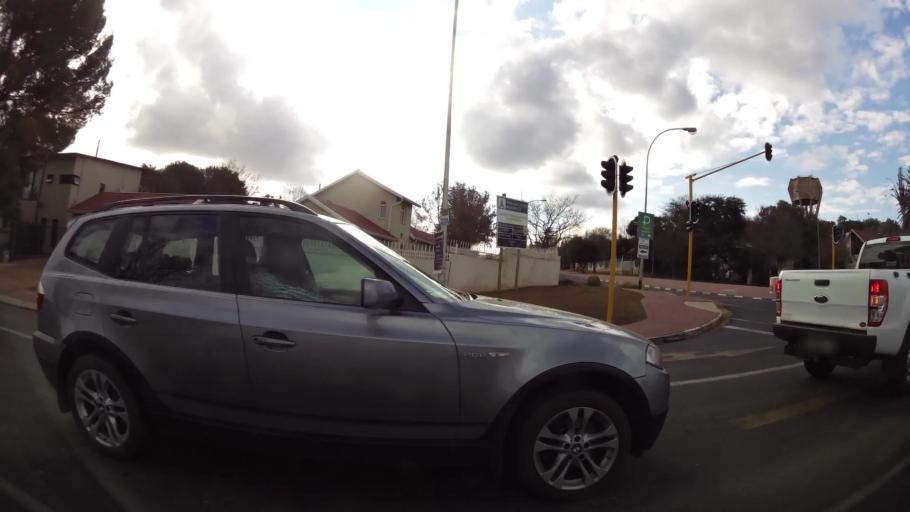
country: ZA
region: Orange Free State
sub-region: Mangaung Metropolitan Municipality
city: Bloemfontein
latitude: -29.0802
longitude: 26.2069
